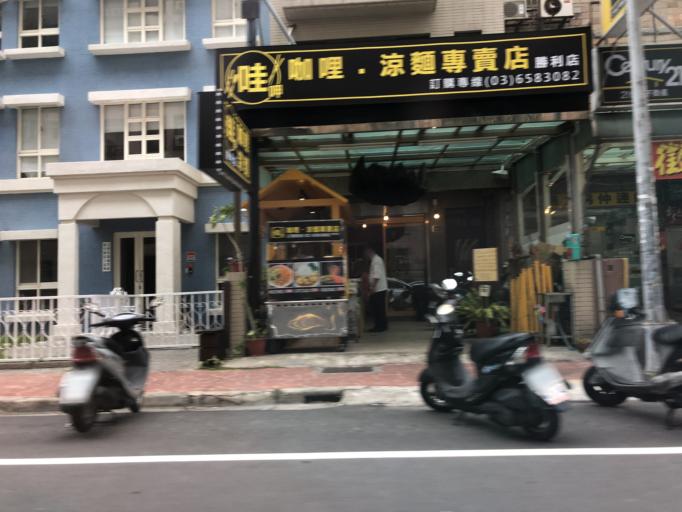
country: TW
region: Taiwan
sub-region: Hsinchu
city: Zhubei
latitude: 24.8228
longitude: 121.0260
